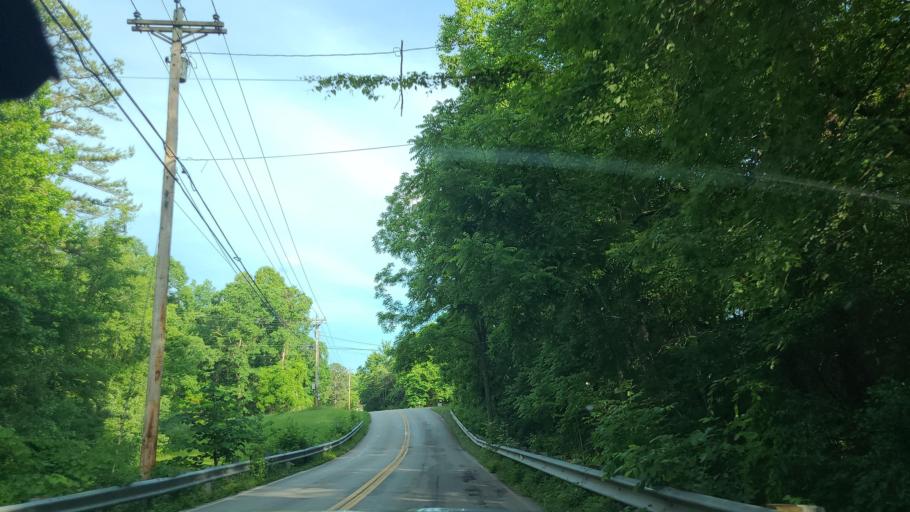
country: US
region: Kentucky
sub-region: Whitley County
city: Corbin
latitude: 36.8894
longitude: -84.2190
